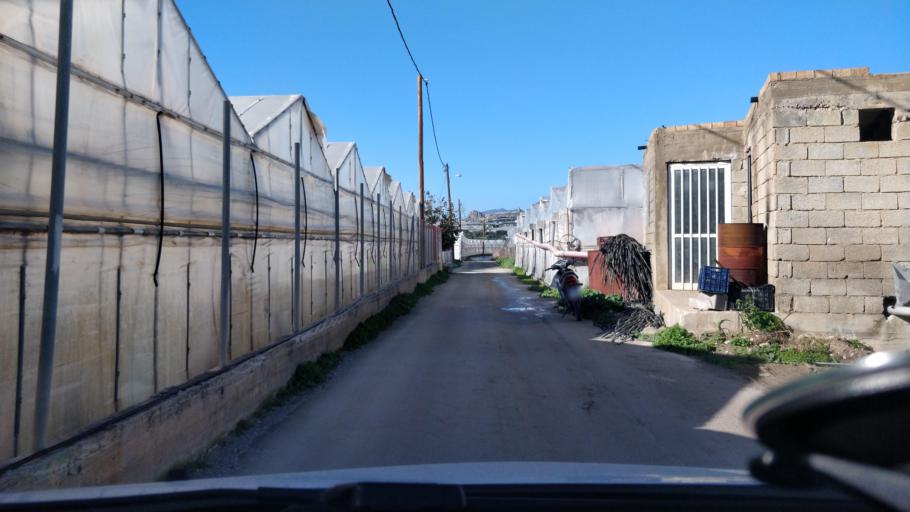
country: GR
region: Crete
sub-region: Nomos Lasithiou
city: Gra Liyia
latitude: 35.0202
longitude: 25.6778
